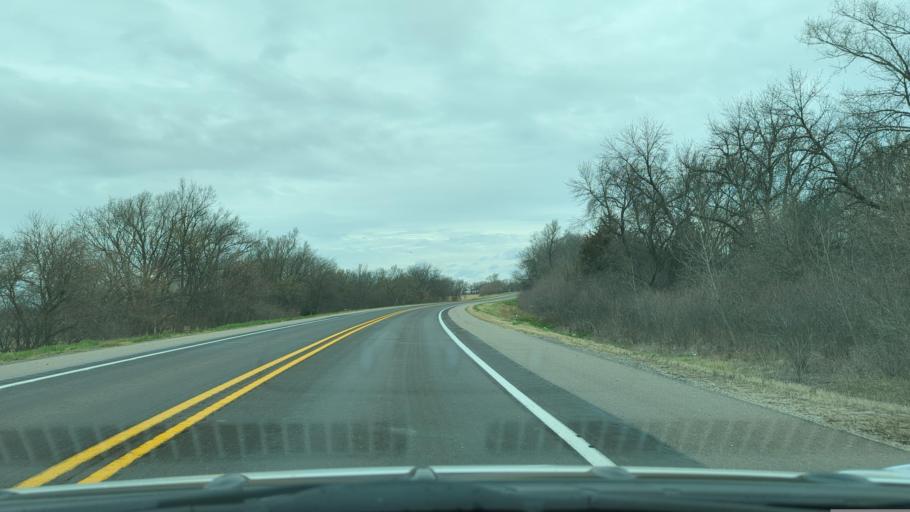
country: US
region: Nebraska
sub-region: Lancaster County
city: Waverly
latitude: 40.9511
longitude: -96.4537
